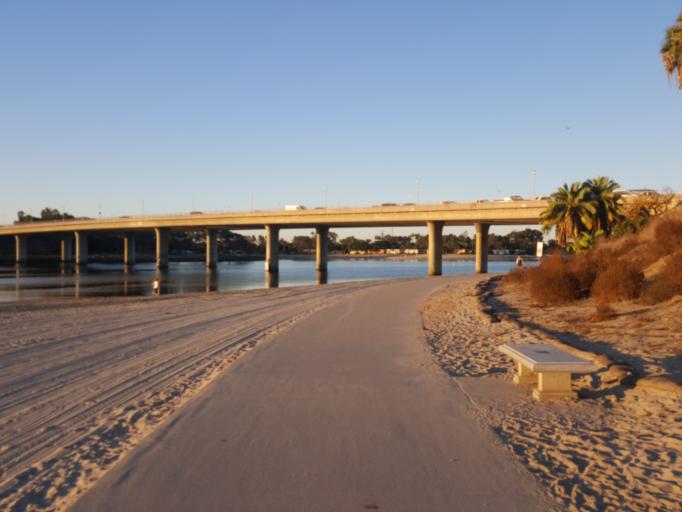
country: US
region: California
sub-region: San Diego County
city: La Jolla
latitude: 32.7802
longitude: -117.2352
